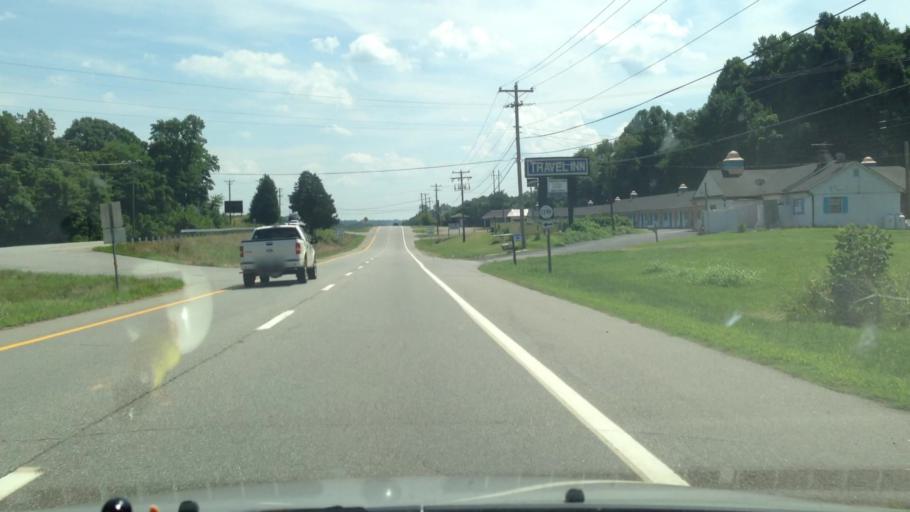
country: US
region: Virginia
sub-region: Henry County
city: Chatmoss
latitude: 36.6329
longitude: -79.8592
